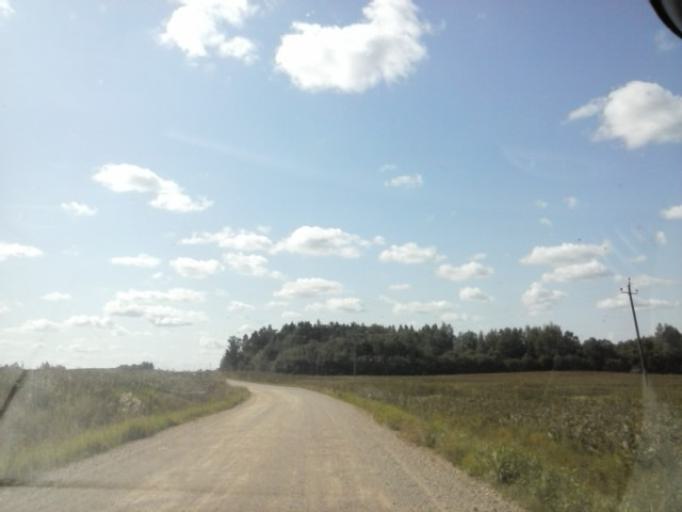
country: EE
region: Polvamaa
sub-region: Polva linn
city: Polva
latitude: 58.1062
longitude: 26.8582
